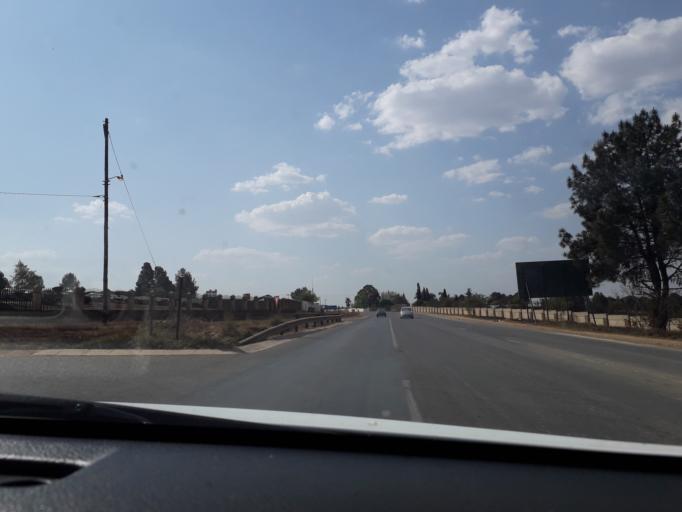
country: ZA
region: Gauteng
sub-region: Ekurhuleni Metropolitan Municipality
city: Tembisa
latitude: -26.0779
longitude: 28.2852
